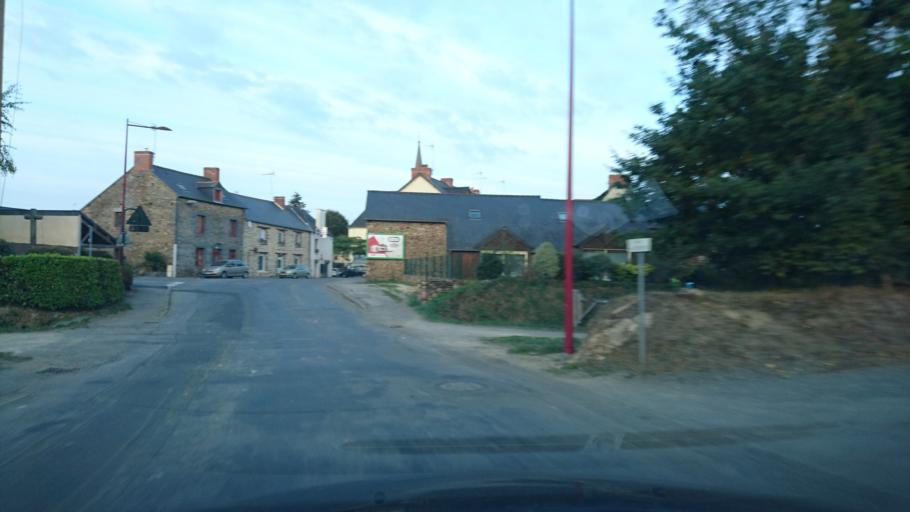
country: FR
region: Brittany
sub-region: Departement d'Ille-et-Vilaine
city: Maure-de-Bretagne
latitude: 47.8902
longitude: -1.9923
